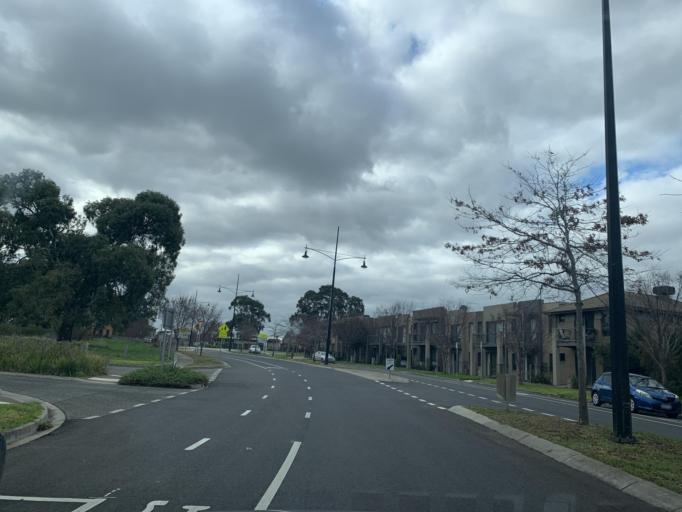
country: AU
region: Victoria
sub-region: Whittlesea
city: Epping
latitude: -37.6304
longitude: 145.0220
